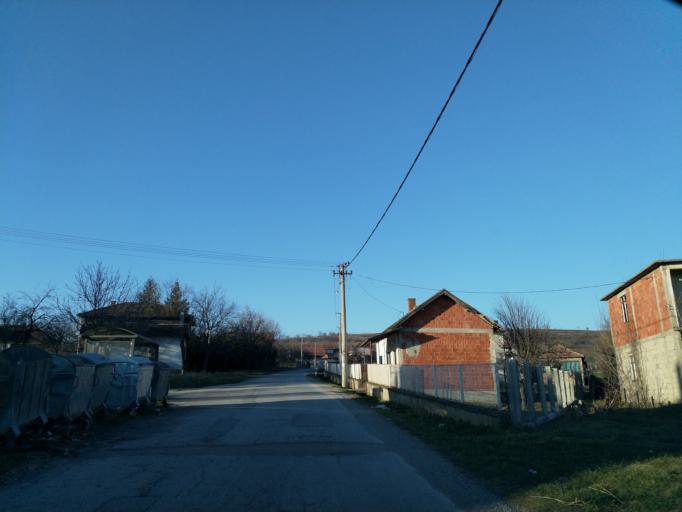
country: RS
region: Central Serbia
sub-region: Pomoravski Okrug
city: Paracin
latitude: 43.9190
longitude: 21.5106
